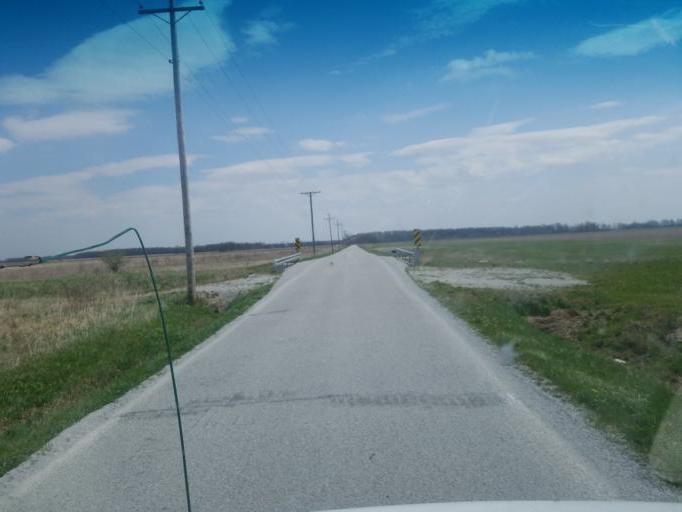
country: US
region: Ohio
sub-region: Hardin County
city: Forest
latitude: 40.7596
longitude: -83.5065
